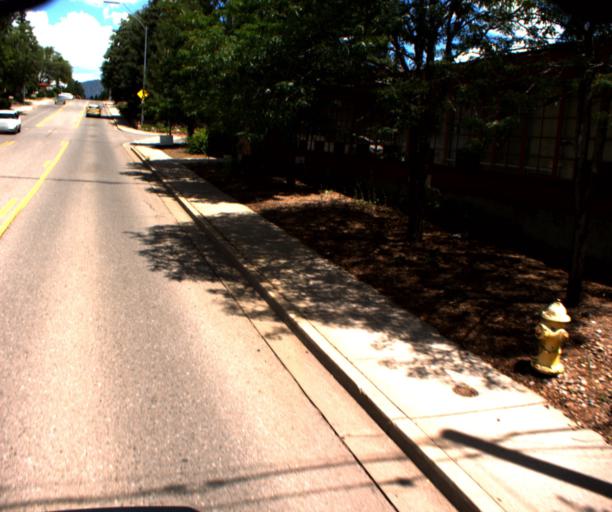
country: US
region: Arizona
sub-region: Coconino County
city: Flagstaff
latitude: 35.2015
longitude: -111.6498
